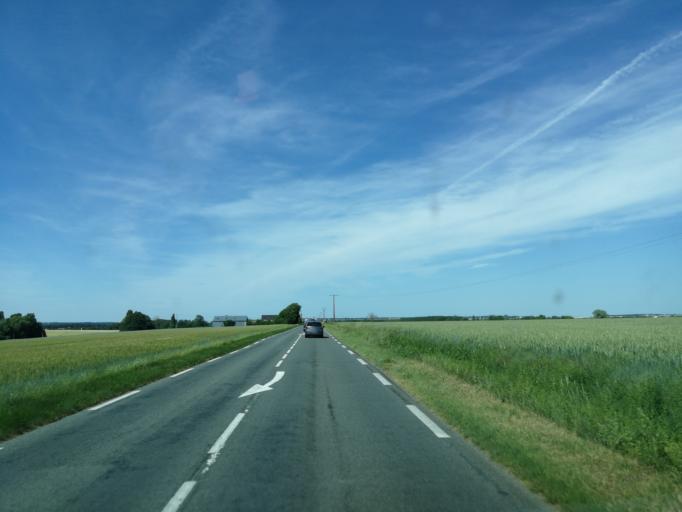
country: FR
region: Poitou-Charentes
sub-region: Departement de la Vienne
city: Loudun
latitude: 47.0685
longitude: 0.1675
